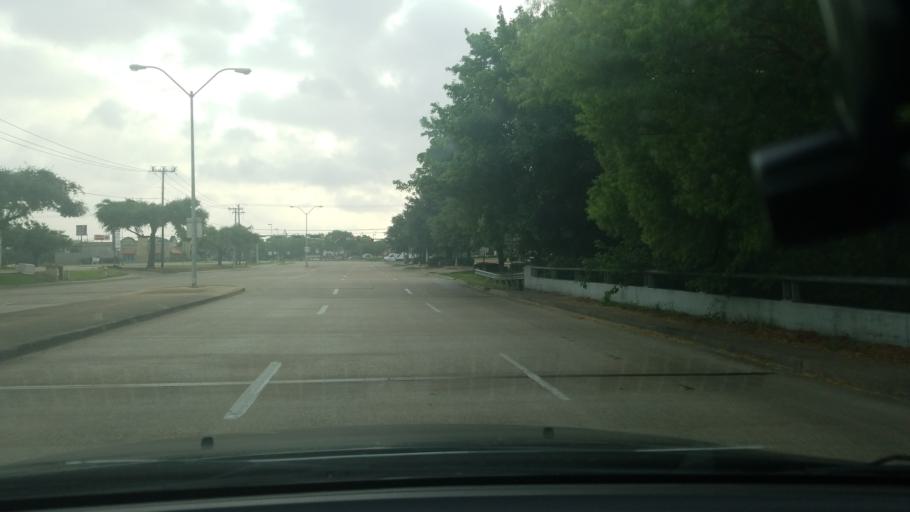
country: US
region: Texas
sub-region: Dallas County
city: Mesquite
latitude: 32.7822
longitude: -96.6279
